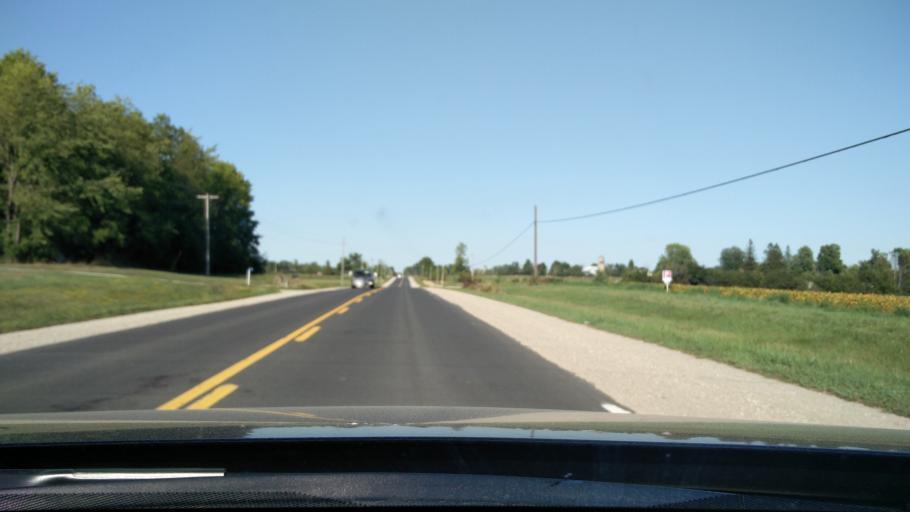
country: CA
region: Ontario
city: Perth
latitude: 44.8649
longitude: -76.2839
